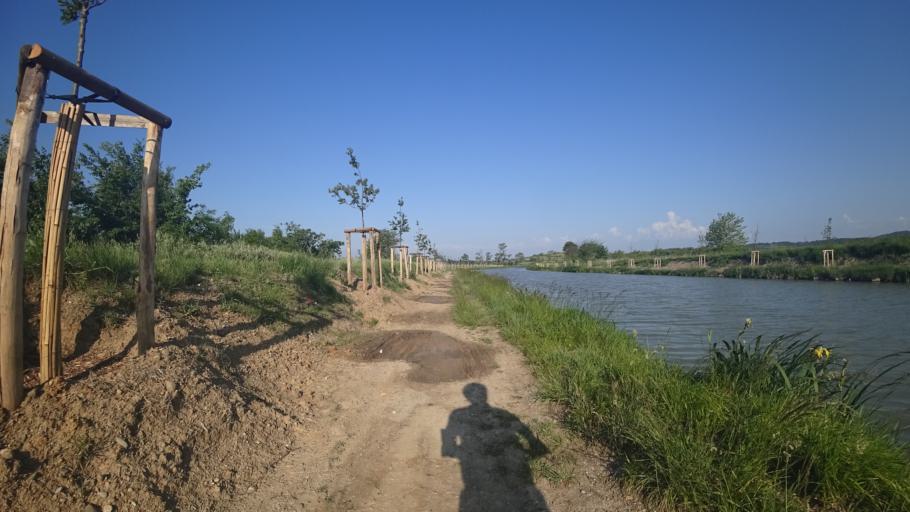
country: FR
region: Languedoc-Roussillon
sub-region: Departement de l'Aude
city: Lezignan-Corbieres
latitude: 43.2420
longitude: 2.7922
